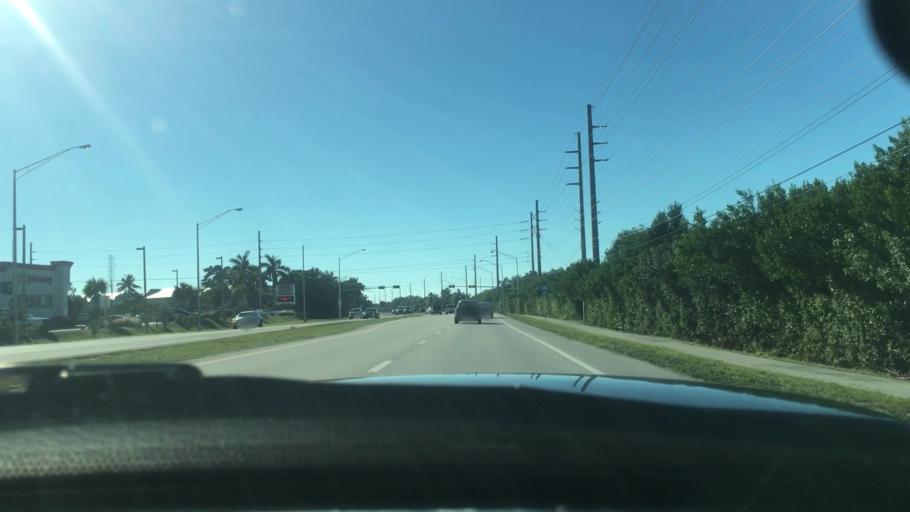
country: US
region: Florida
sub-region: Monroe County
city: Stock Island
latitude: 24.5748
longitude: -81.7358
